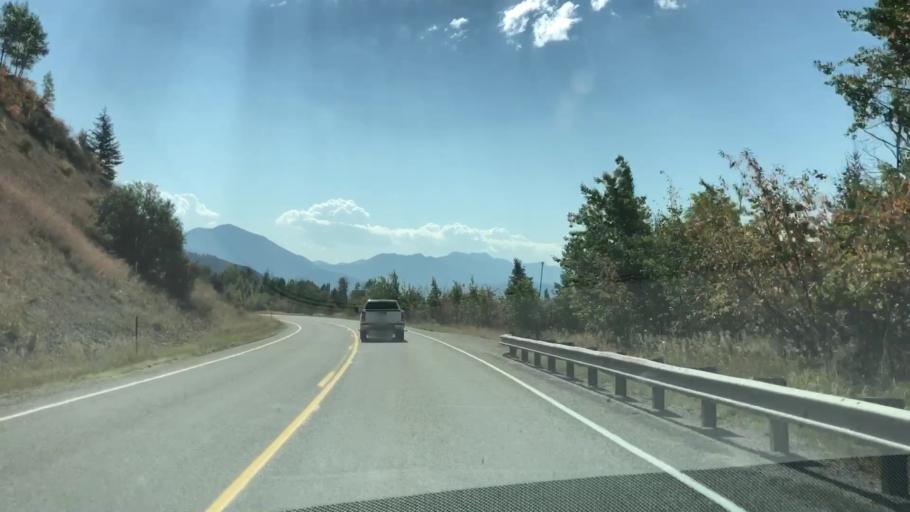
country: US
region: Wyoming
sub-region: Teton County
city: Hoback
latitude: 43.2286
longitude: -111.0874
